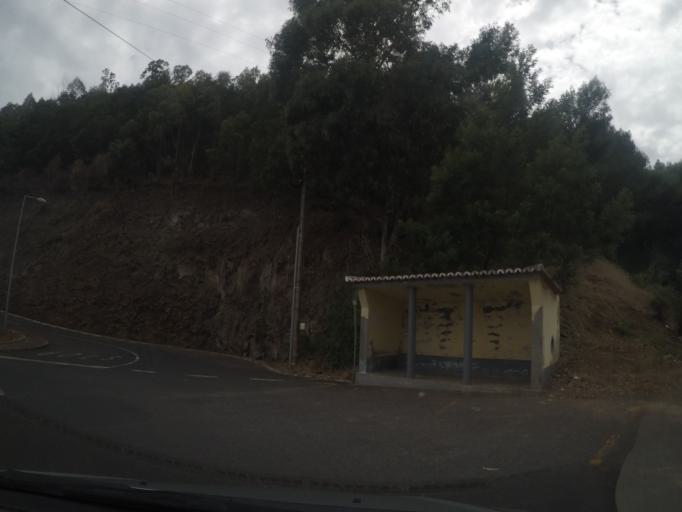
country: PT
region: Madeira
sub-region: Santa Cruz
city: Santa Cruz
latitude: 32.6870
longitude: -16.8140
